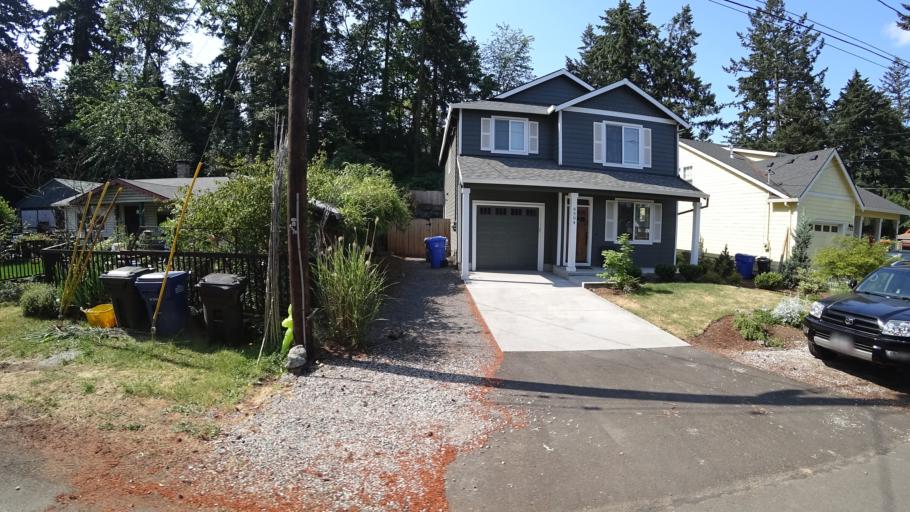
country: US
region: Oregon
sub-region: Multnomah County
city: Lents
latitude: 45.4536
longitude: -122.5955
